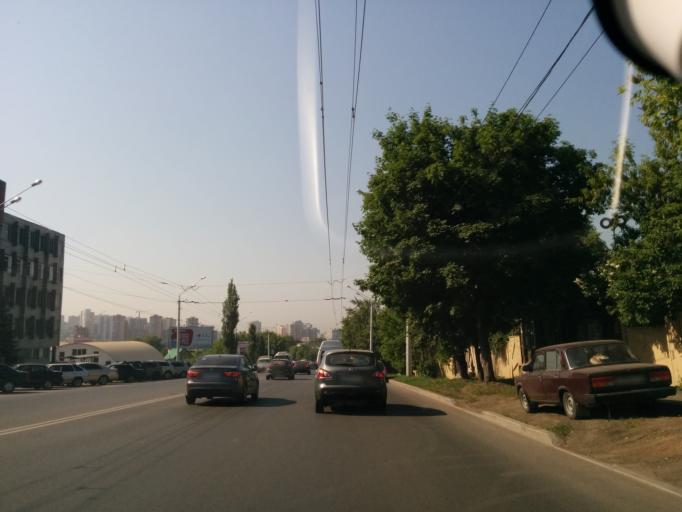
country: RU
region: Bashkortostan
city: Ufa
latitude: 54.7258
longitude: 55.9761
